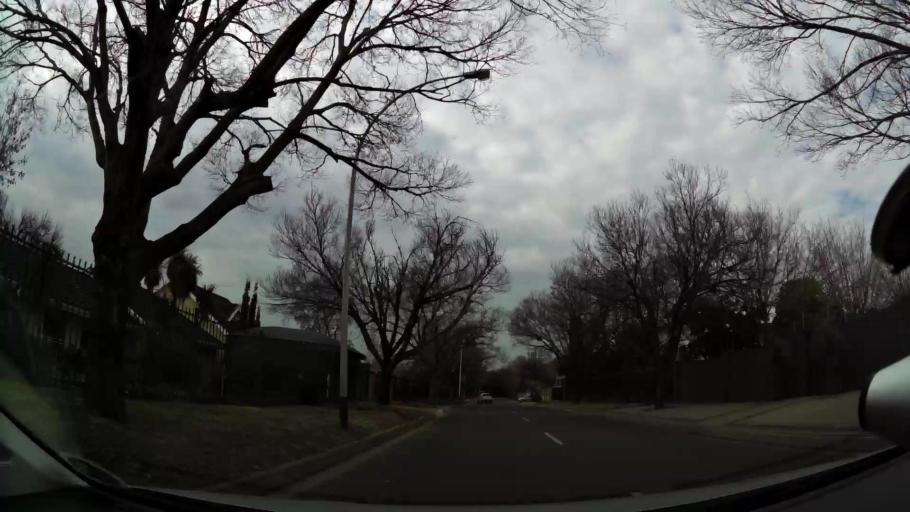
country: ZA
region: Orange Free State
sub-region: Mangaung Metropolitan Municipality
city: Bloemfontein
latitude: -29.0908
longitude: 26.2110
